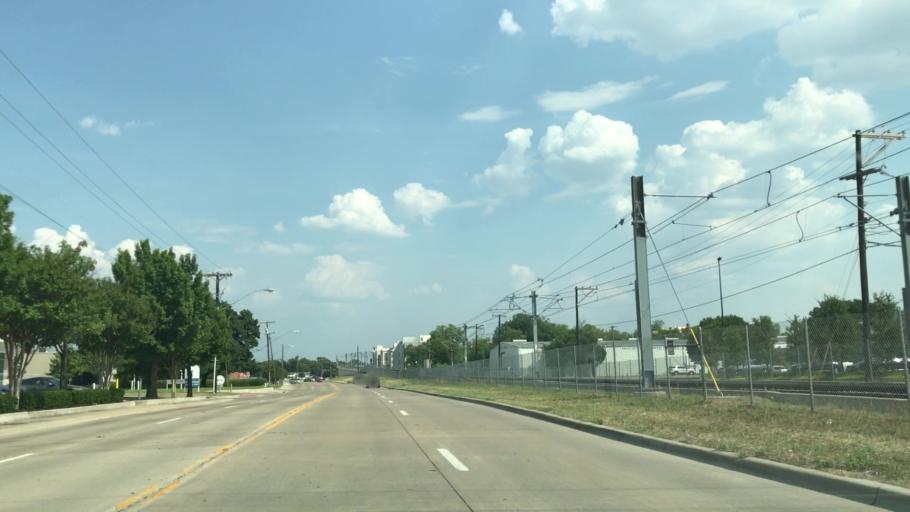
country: US
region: Texas
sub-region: Dallas County
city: University Park
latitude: 32.8273
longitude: -96.8382
